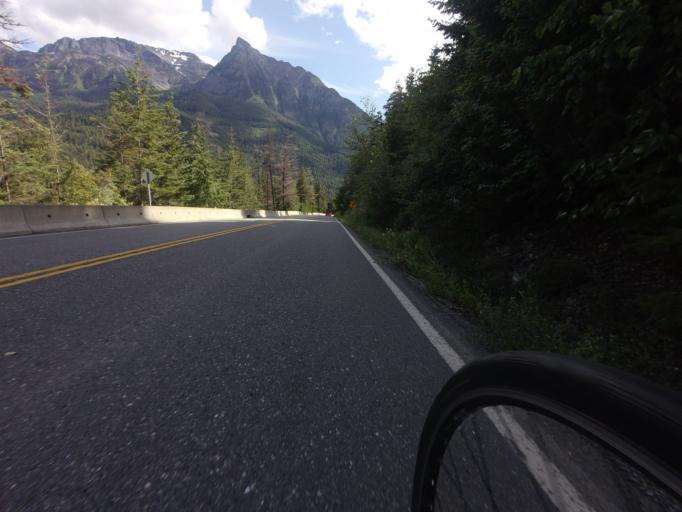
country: CA
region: British Columbia
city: Lillooet
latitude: 50.6471
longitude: -122.0224
